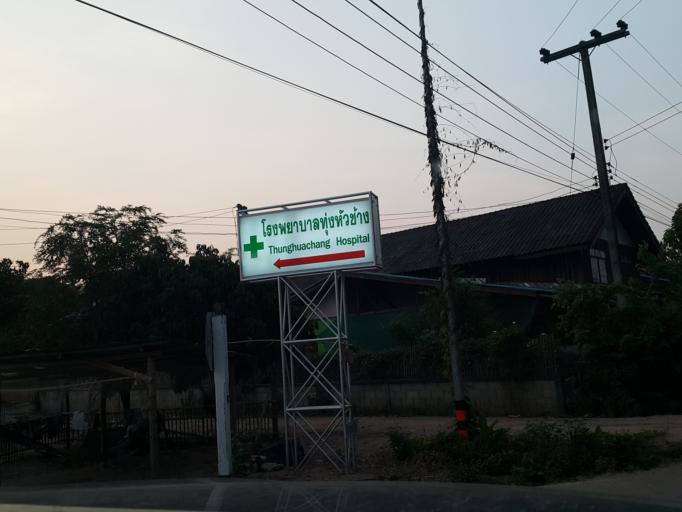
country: TH
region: Lamphun
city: Thung Hua Chang
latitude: 17.9948
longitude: 99.0306
